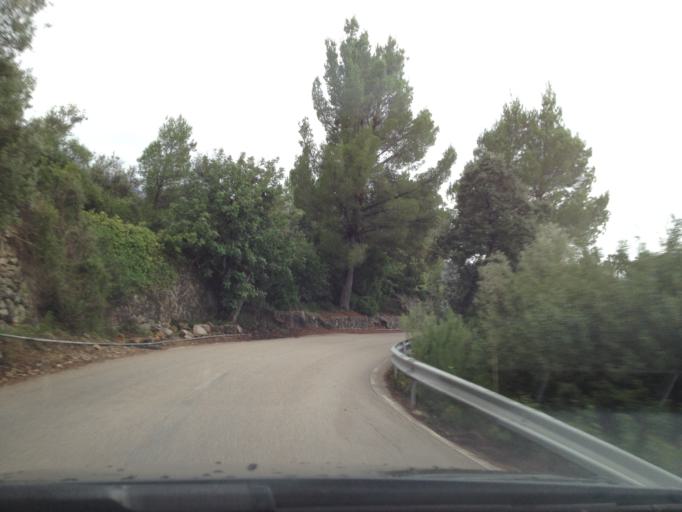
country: ES
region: Balearic Islands
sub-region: Illes Balears
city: Deia
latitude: 39.7663
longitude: 2.6572
